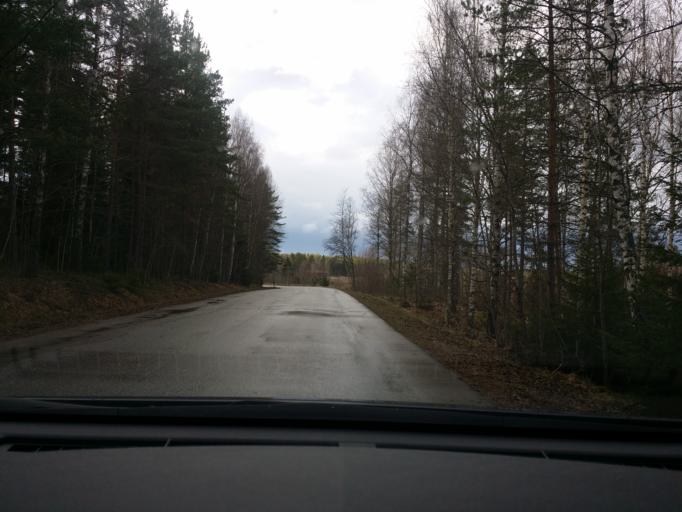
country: SE
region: Soedermanland
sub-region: Eskilstuna Kommun
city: Arla
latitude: 59.2980
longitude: 16.6873
